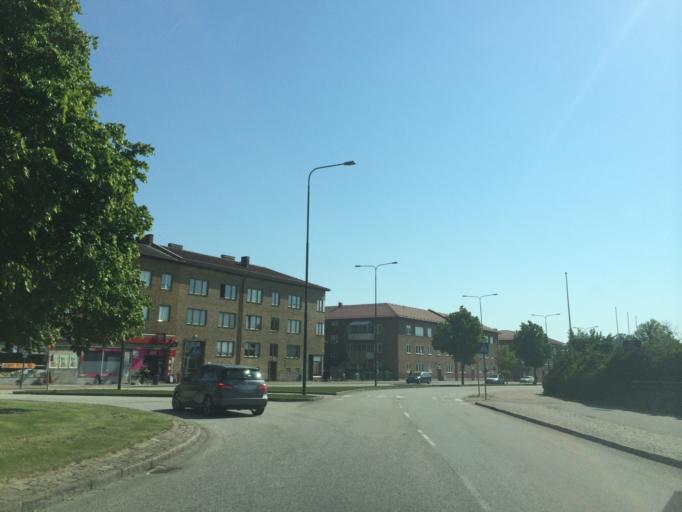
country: SE
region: Skane
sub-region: Burlovs Kommun
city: Arloev
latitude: 55.6148
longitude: 13.0424
